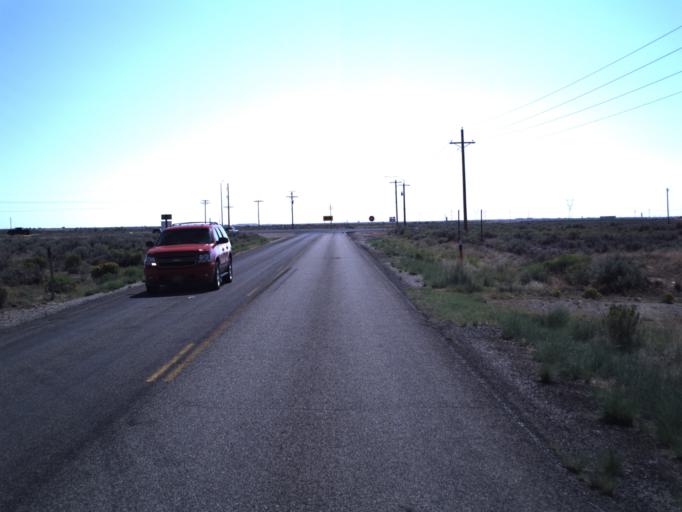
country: US
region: Utah
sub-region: Duchesne County
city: Duchesne
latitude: 40.2482
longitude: -110.3895
